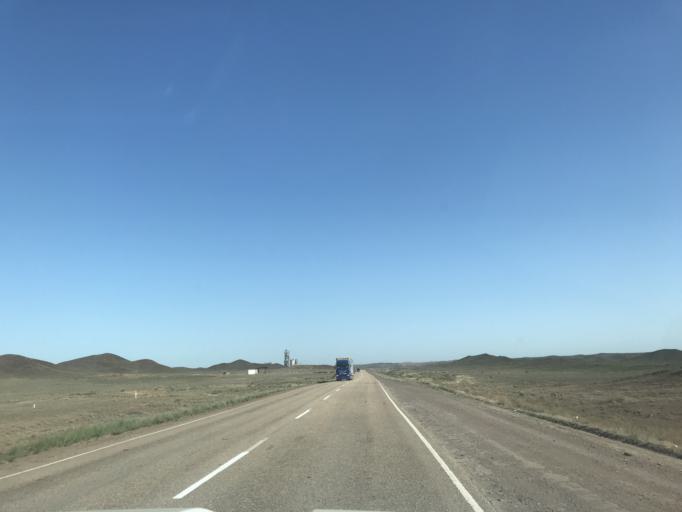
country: KZ
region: Zhambyl
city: Mynaral
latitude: 45.4067
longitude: 73.6329
